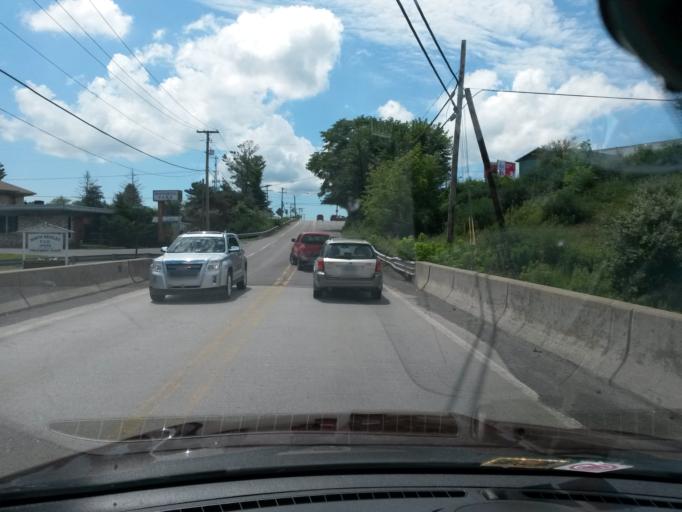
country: US
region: West Virginia
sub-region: Raleigh County
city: Beckley
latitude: 37.7951
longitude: -81.1726
